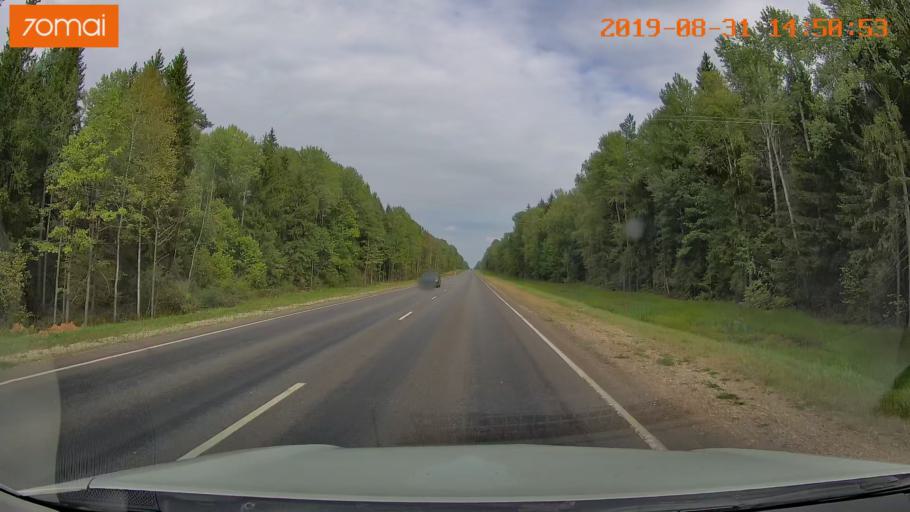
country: RU
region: Kaluga
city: Spas-Demensk
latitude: 54.2647
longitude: 33.8011
